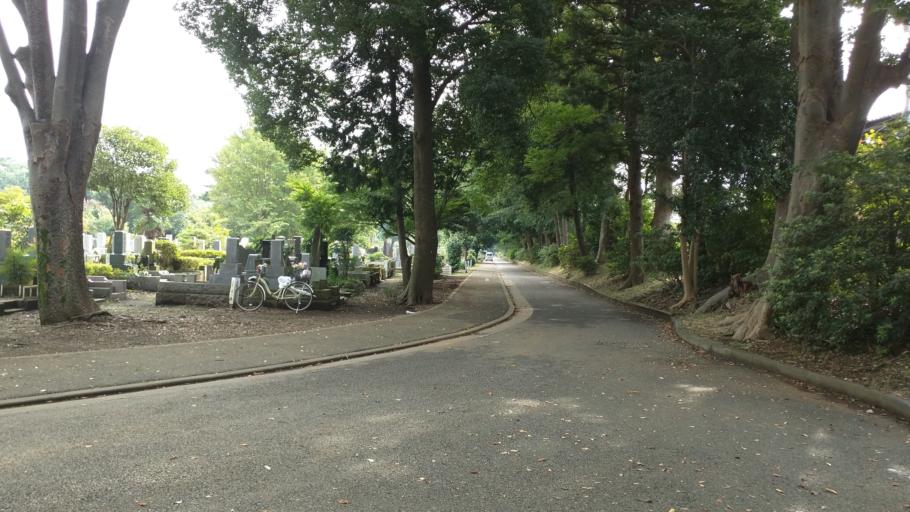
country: JP
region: Tokyo
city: Kokubunji
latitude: 35.6790
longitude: 139.5073
